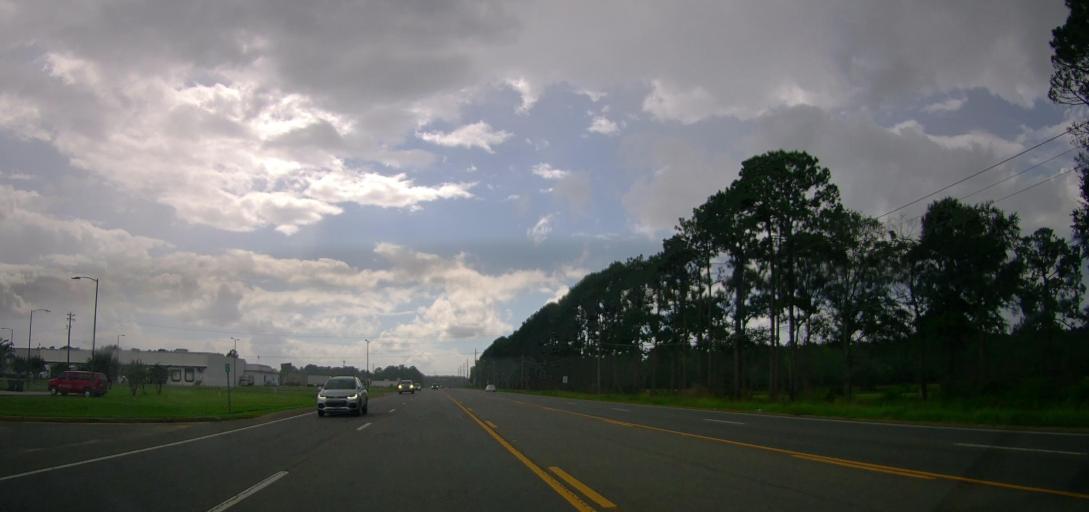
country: US
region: Georgia
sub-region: Coffee County
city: Douglas
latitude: 31.4879
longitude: -82.8549
